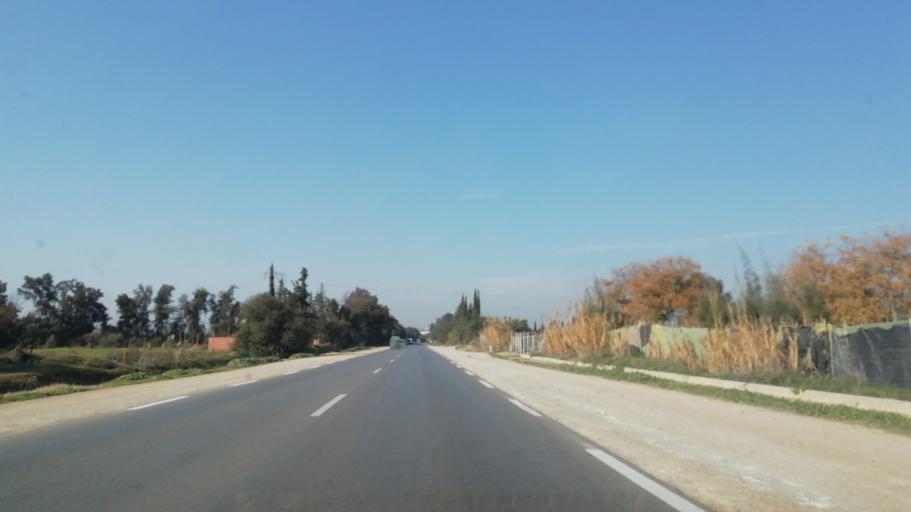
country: DZ
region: Relizane
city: Relizane
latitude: 35.7227
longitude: 0.4944
